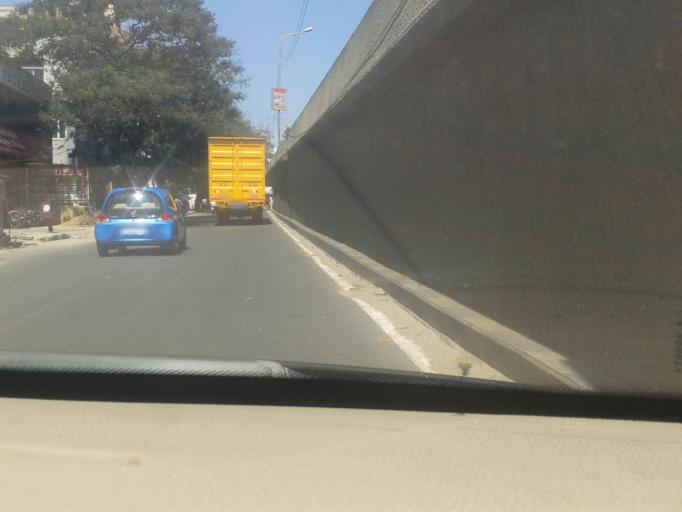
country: IN
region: Karnataka
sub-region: Bangalore Urban
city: Bangalore
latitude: 12.9603
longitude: 77.5938
